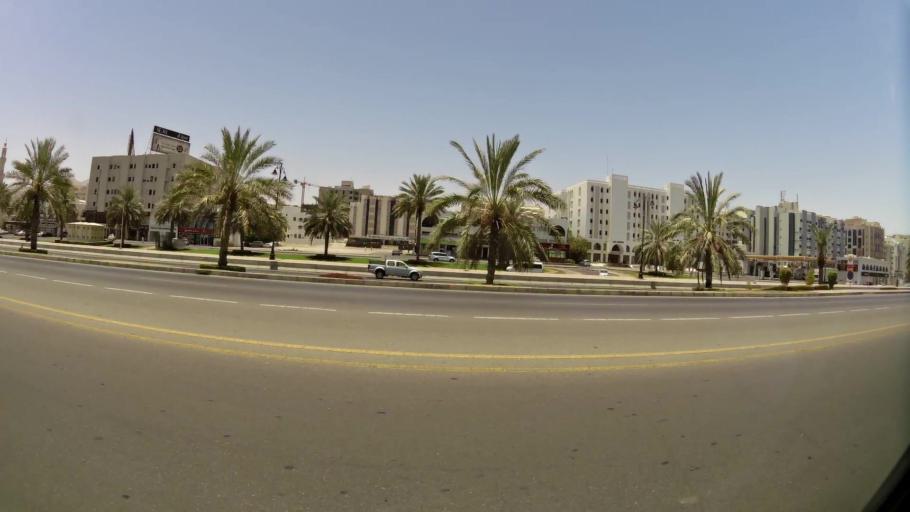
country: OM
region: Muhafazat Masqat
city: Bawshar
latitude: 23.5975
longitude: 58.4202
